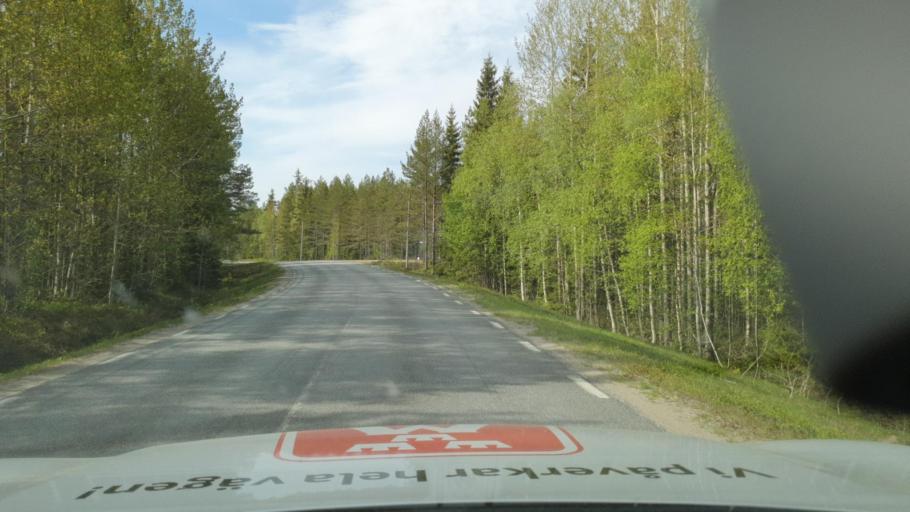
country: SE
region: Vaesterbotten
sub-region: Umea Kommun
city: Roback
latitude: 63.6886
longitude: 20.1380
